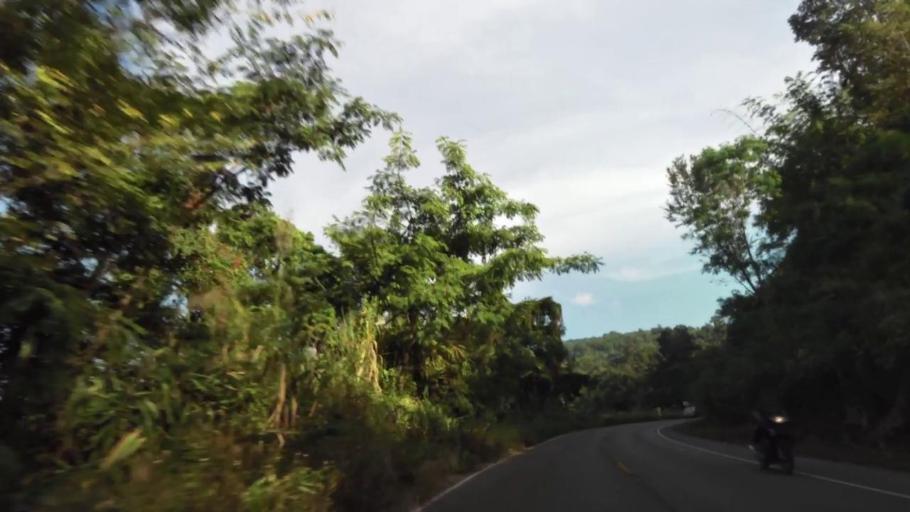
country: TH
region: Chiang Rai
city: Khun Tan
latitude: 19.8630
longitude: 100.4254
